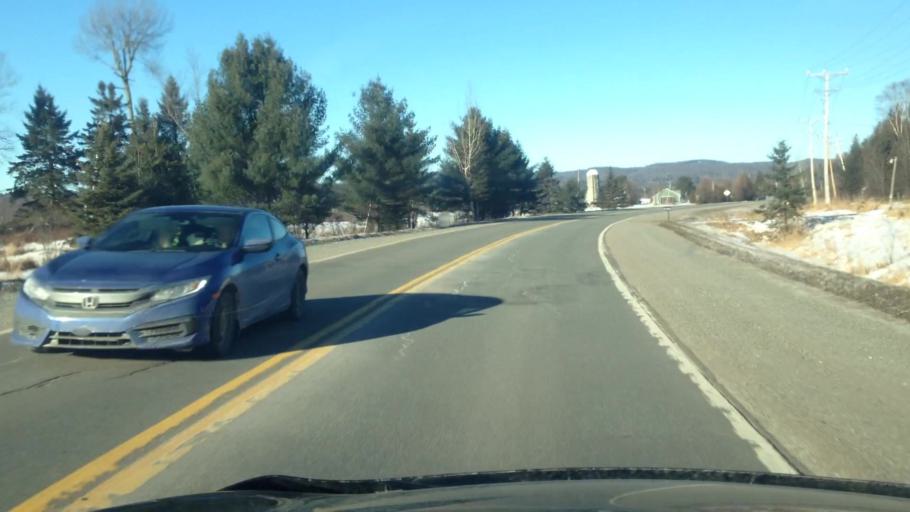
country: CA
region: Quebec
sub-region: Laurentides
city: Mont-Tremblant
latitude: 46.0603
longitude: -74.6217
